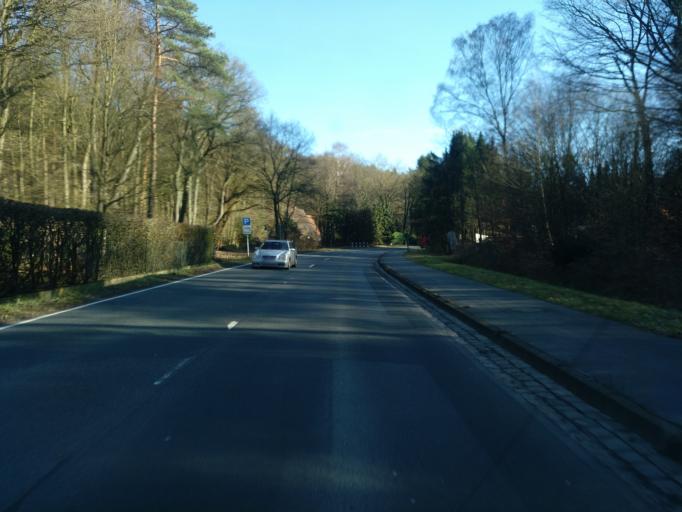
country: DE
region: Hamburg
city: Harburg
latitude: 53.4530
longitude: 9.9034
